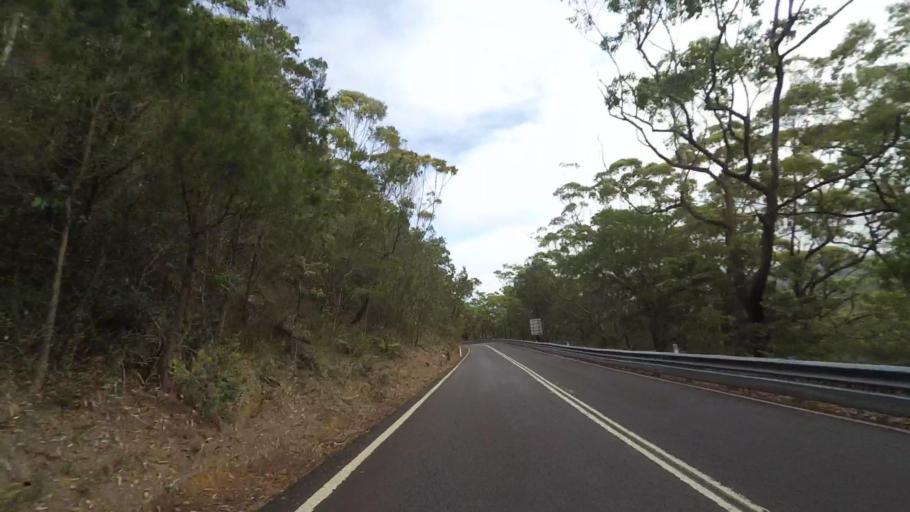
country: AU
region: New South Wales
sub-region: Wollongong
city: Helensburgh
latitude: -34.2178
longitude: 150.9991
